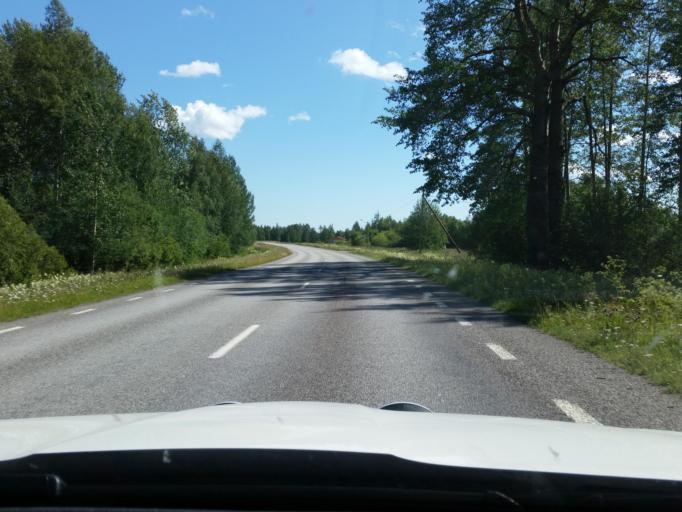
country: SE
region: Norrbotten
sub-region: Alvsbyns Kommun
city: AElvsbyn
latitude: 65.6932
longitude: 20.5974
